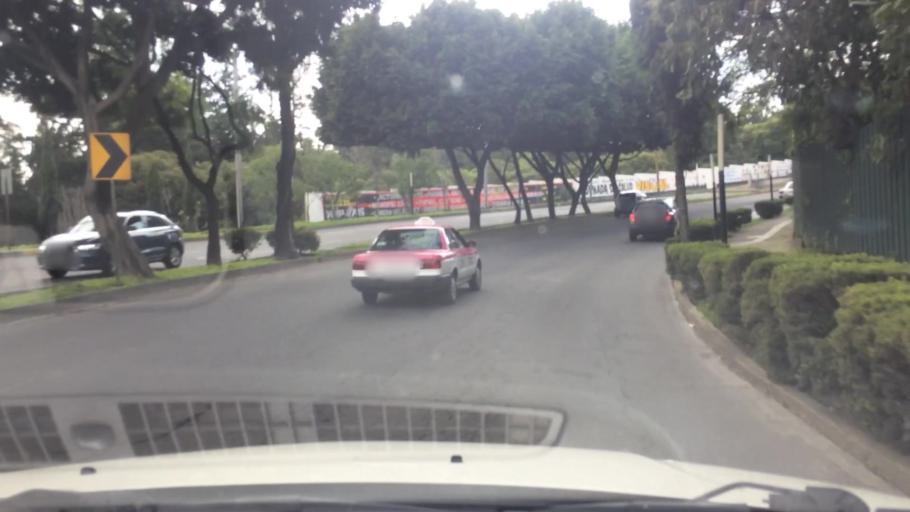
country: MX
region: Mexico City
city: Alvaro Obregon
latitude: 19.3515
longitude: -99.2053
